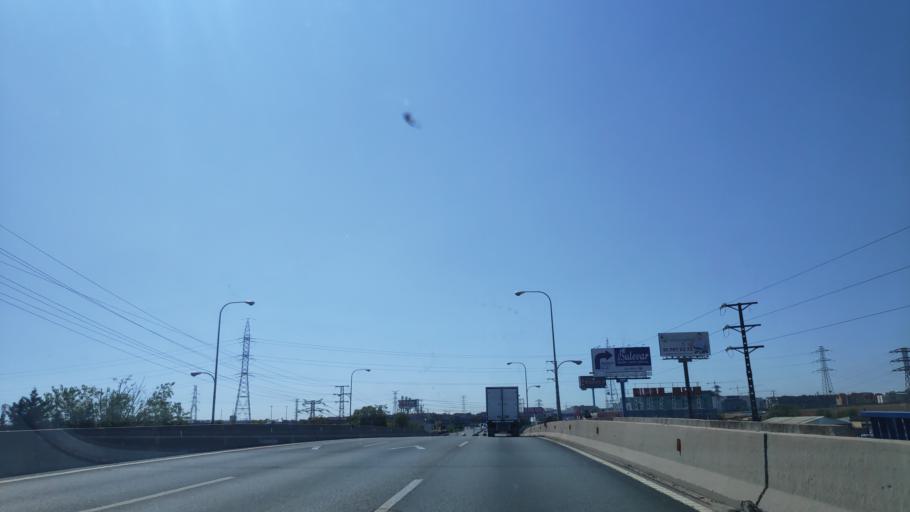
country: ES
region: Madrid
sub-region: Provincia de Madrid
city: Villaverde
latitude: 40.3381
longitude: -3.7245
